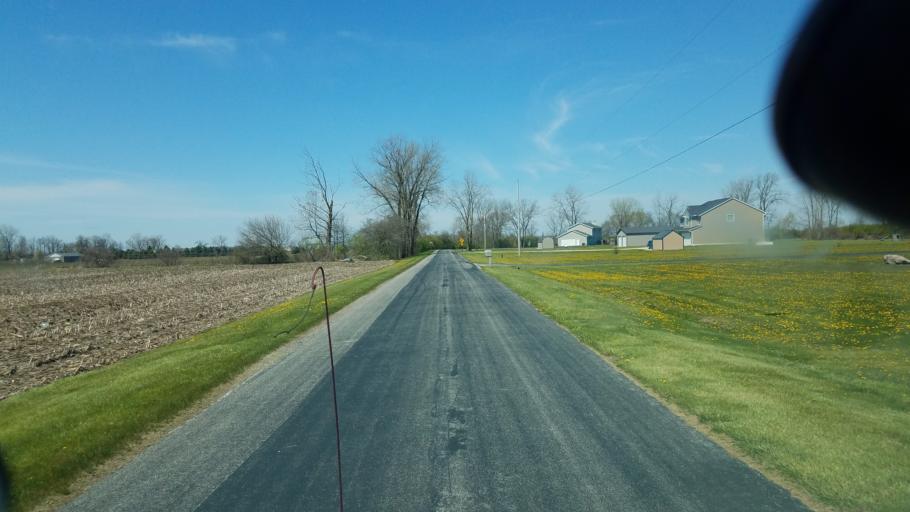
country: US
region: Ohio
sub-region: Marion County
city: Marion
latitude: 40.6355
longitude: -83.0898
